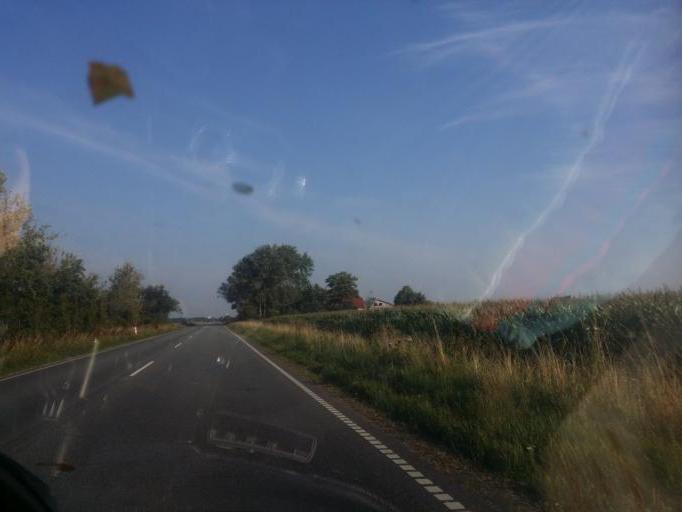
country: DK
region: South Denmark
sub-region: Tonder Kommune
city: Sherrebek
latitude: 55.1741
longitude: 8.7496
